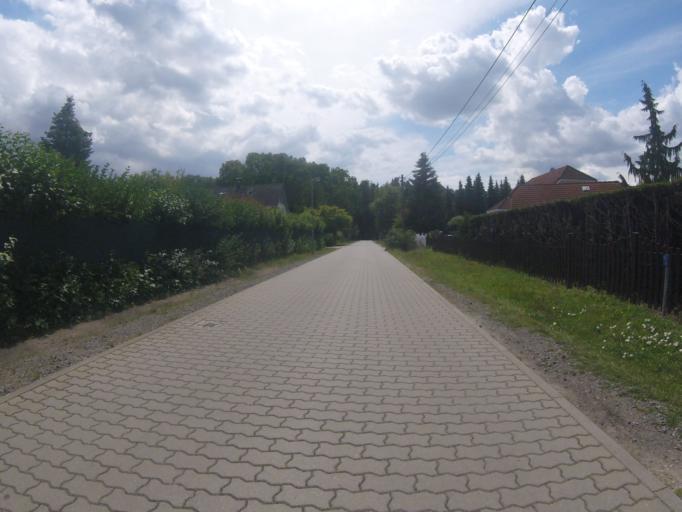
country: DE
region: Brandenburg
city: Bestensee
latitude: 52.2504
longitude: 13.6377
